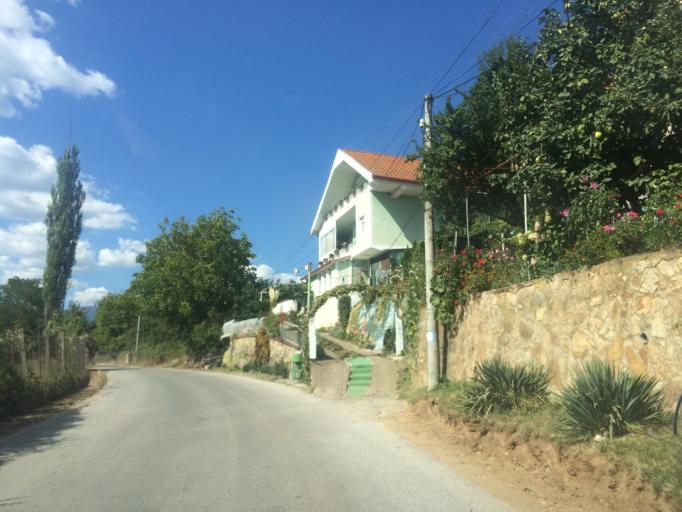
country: MK
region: Makedonska Kamenica
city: Makedonska Kamenica
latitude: 42.0282
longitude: 22.5871
